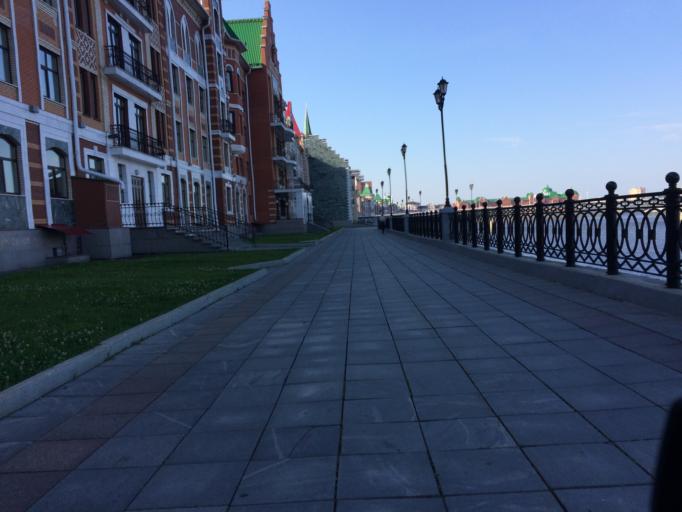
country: RU
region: Mariy-El
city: Yoshkar-Ola
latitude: 56.6347
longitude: 47.9102
